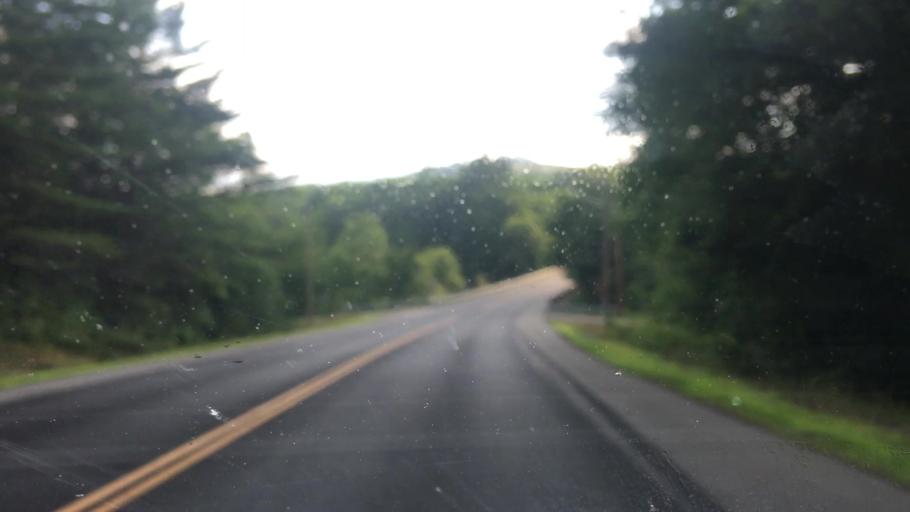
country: US
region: Maine
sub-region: Waldo County
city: Searsmont
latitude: 44.4008
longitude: -69.2888
